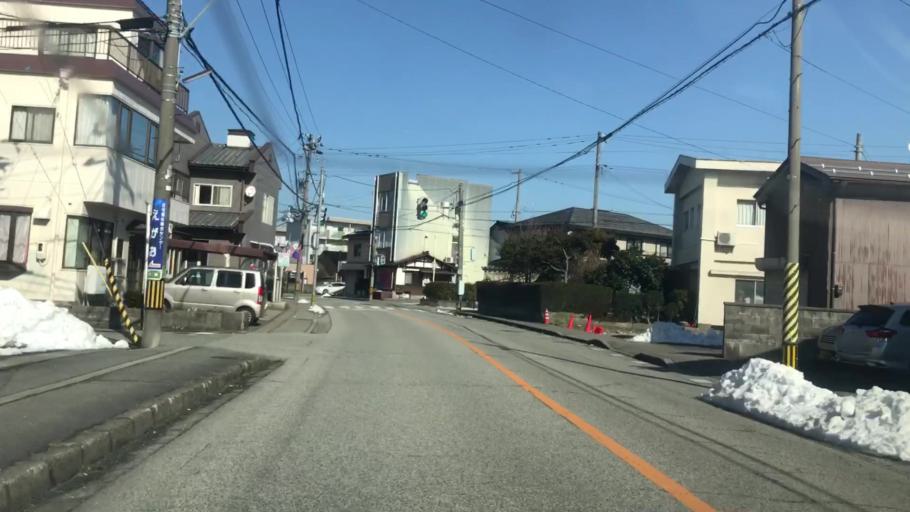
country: JP
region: Toyama
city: Toyama-shi
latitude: 36.6728
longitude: 137.2404
